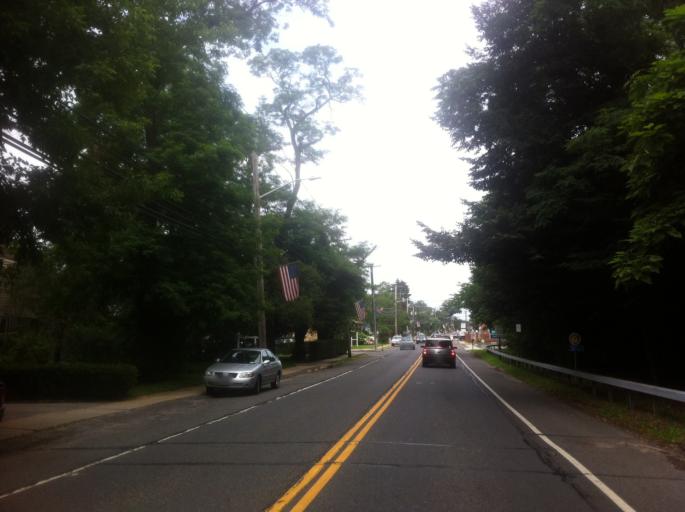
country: US
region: New York
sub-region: Nassau County
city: Locust Valley
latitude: 40.8757
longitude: -73.6031
